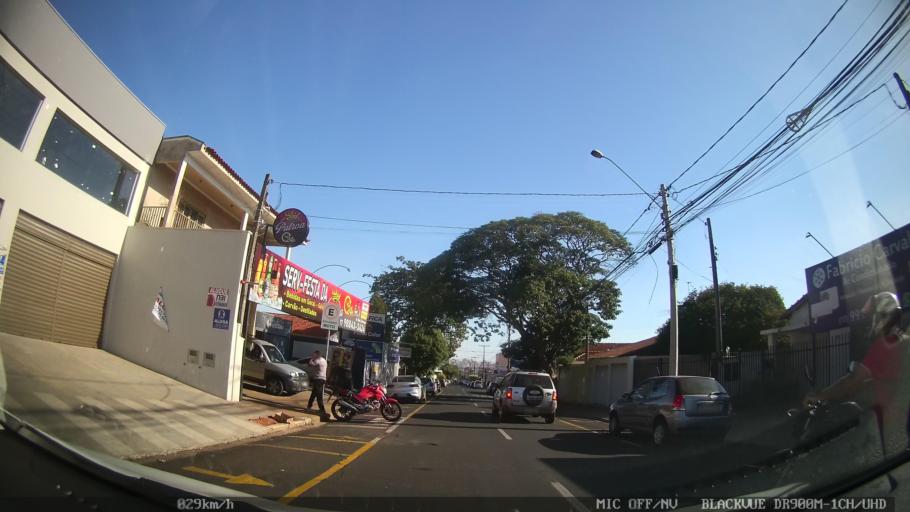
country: BR
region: Sao Paulo
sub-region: Sao Jose Do Rio Preto
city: Sao Jose do Rio Preto
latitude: -20.7961
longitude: -49.3660
